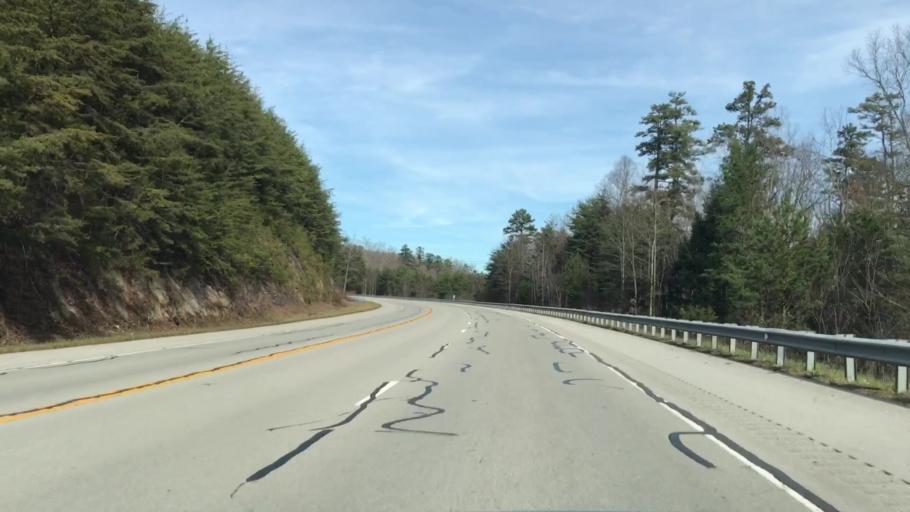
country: US
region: Kentucky
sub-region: McCreary County
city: Whitley City
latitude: 36.8599
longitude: -84.4877
